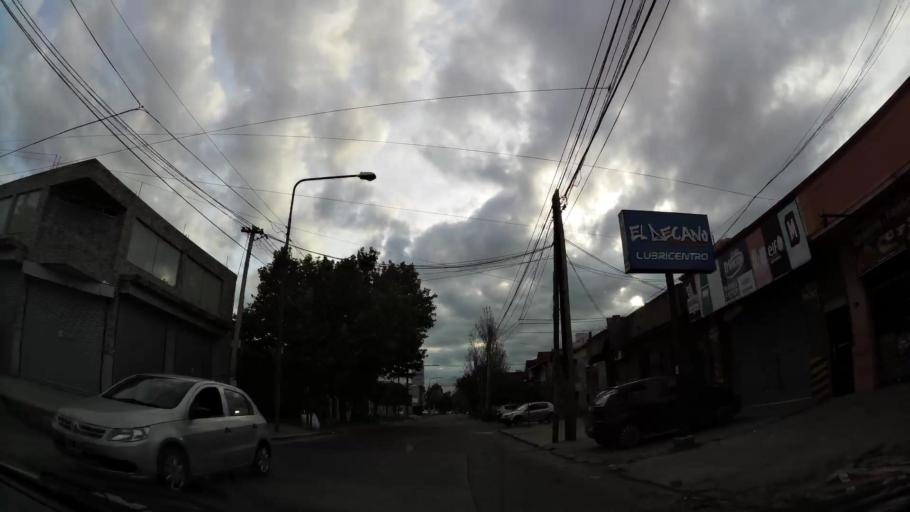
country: AR
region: Buenos Aires
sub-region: Partido de Quilmes
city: Quilmes
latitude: -34.7315
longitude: -58.2474
